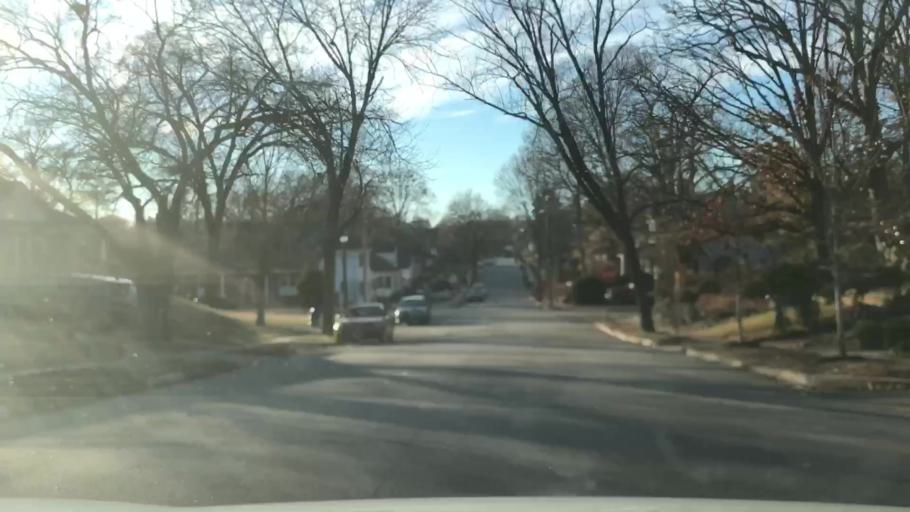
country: US
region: Missouri
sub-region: Saint Louis County
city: Brentwood
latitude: 38.6189
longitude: -90.3444
